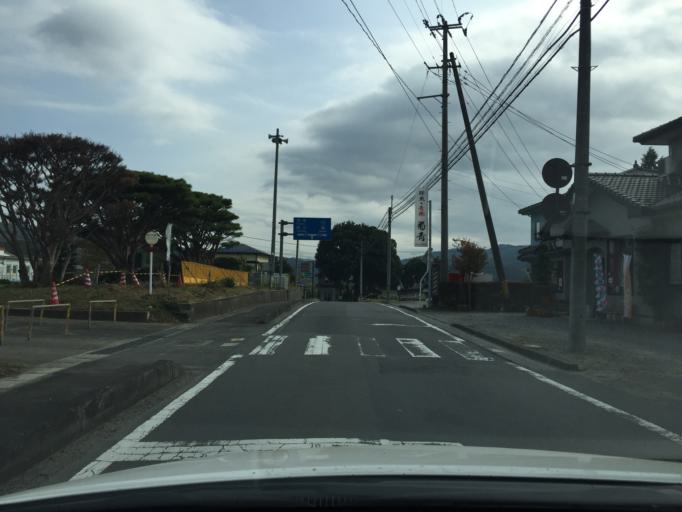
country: JP
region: Fukushima
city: Ishikawa
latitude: 36.9677
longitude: 140.4331
